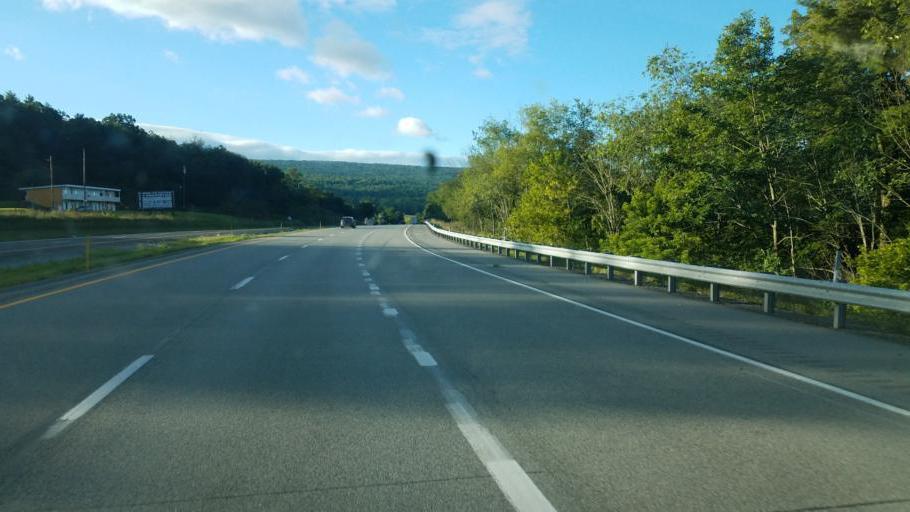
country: US
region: Pennsylvania
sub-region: Bedford County
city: Earlston
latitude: 39.9471
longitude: -78.2292
